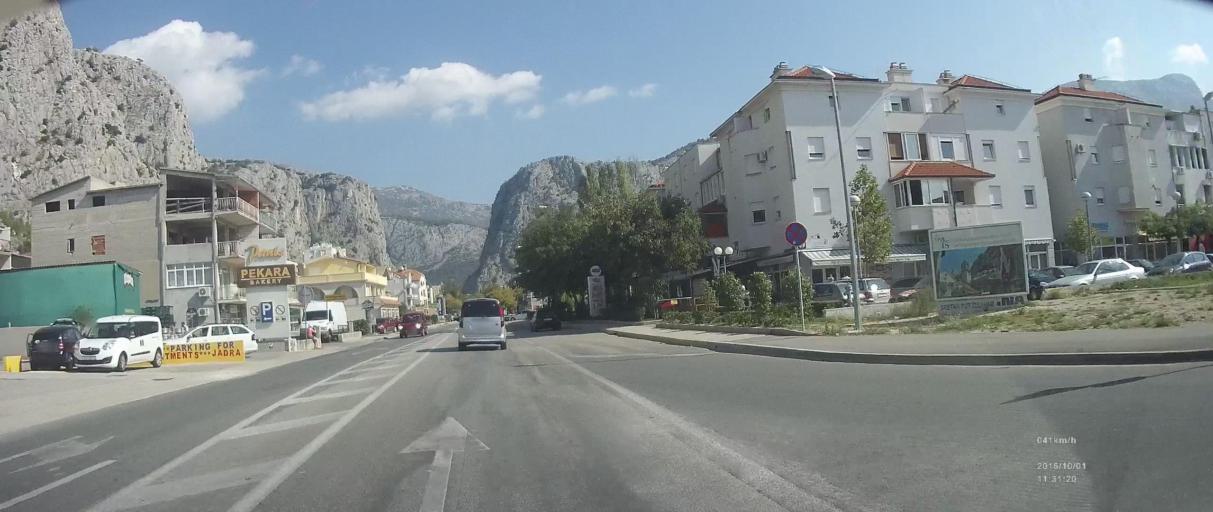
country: HR
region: Splitsko-Dalmatinska
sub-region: Grad Omis
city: Omis
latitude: 43.4432
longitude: 16.6837
